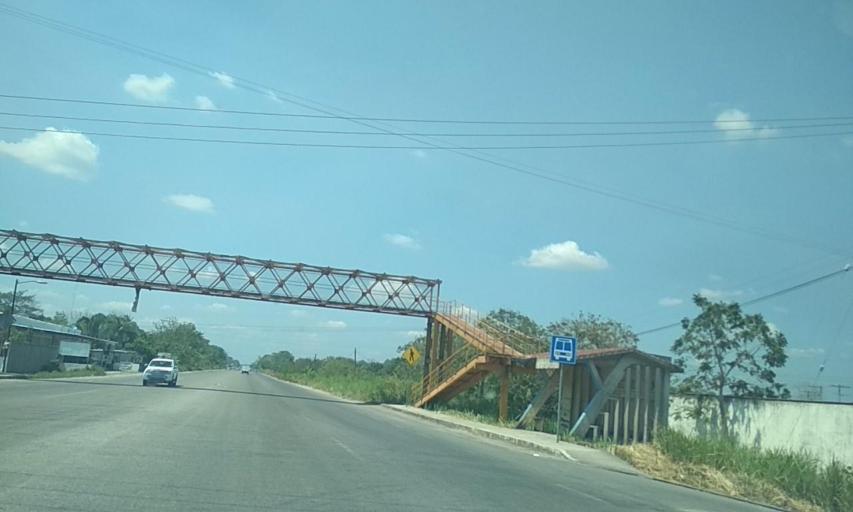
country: MX
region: Tabasco
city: Huimanguillo
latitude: 17.8413
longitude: -93.3977
